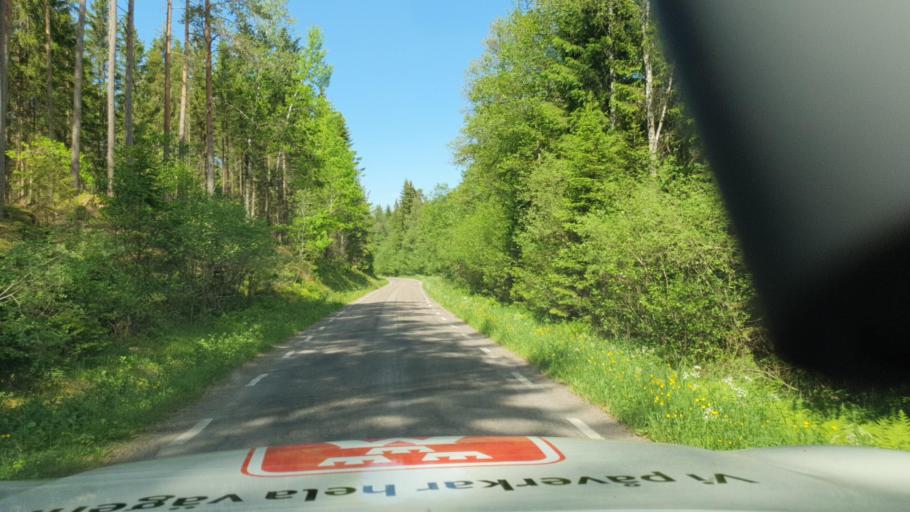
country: SE
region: Vaestra Goetaland
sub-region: Herrljunga Kommun
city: Herrljunga
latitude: 58.1364
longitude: 13.0810
